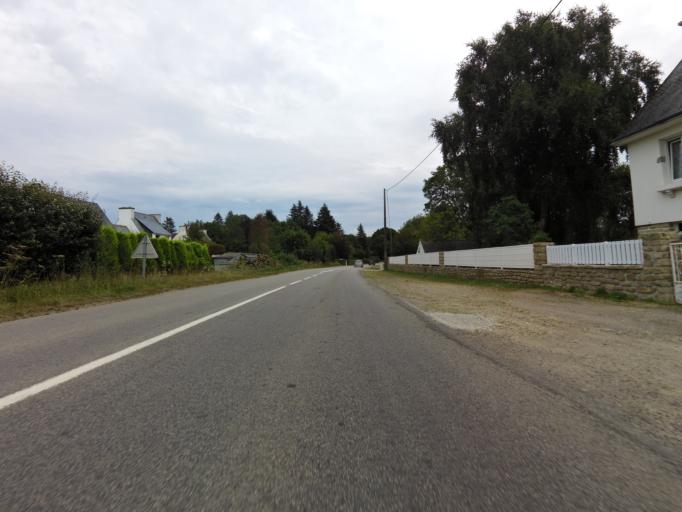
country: FR
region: Brittany
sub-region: Departement du Finistere
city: Douarnenez
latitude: 48.0825
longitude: -4.3697
